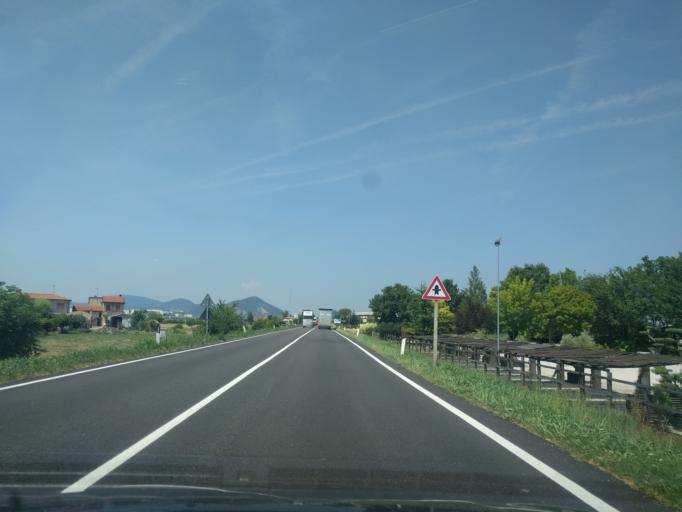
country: IT
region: Veneto
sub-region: Provincia di Padova
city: Solesino
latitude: 45.1915
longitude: 11.7558
